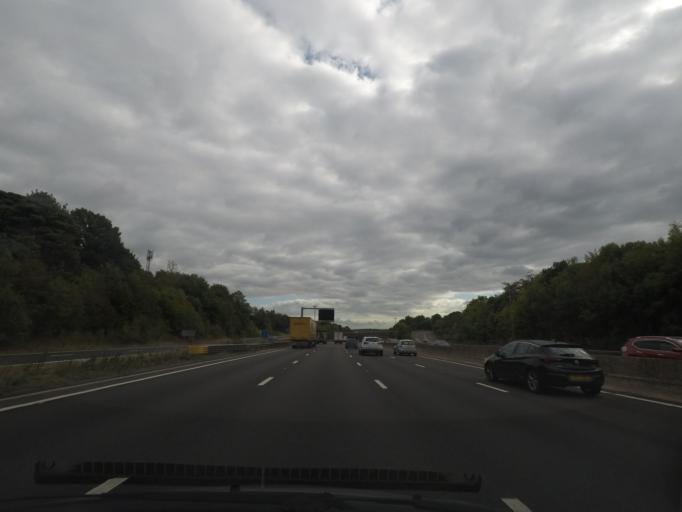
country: GB
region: England
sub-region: Sheffield
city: Chapletown
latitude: 53.4590
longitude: -1.4464
